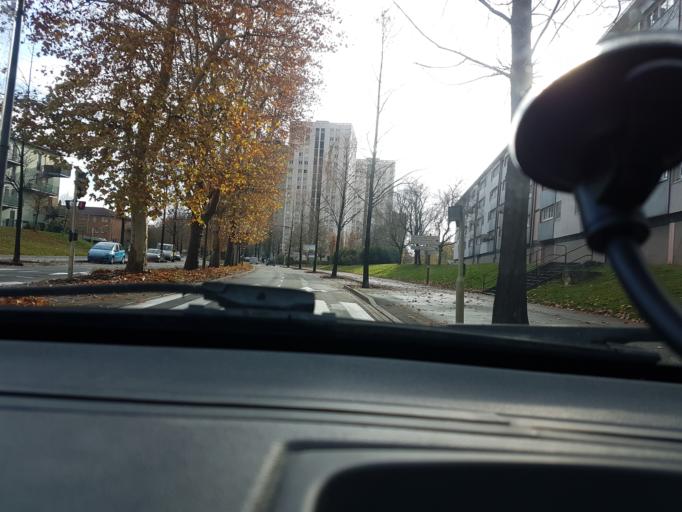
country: FR
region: Franche-Comte
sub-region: Territoire de Belfort
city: Bavilliers
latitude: 47.6347
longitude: 6.8383
